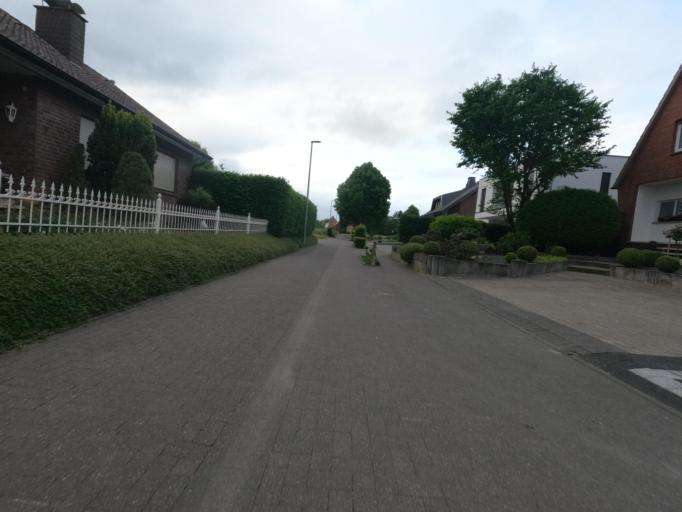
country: NL
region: Limburg
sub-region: Gemeente Roerdalen
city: Vlodrop
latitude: 51.1234
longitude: 6.1057
